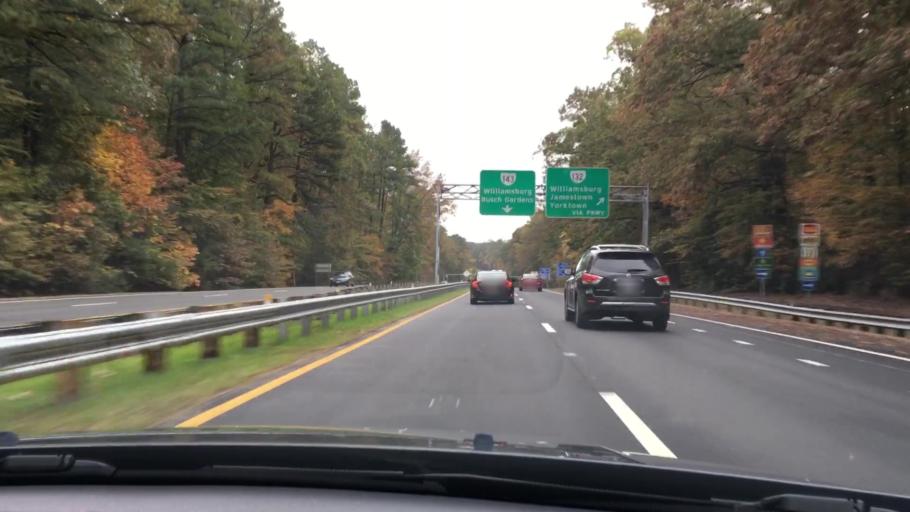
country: US
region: Virginia
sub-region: City of Williamsburg
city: Williamsburg
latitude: 37.2996
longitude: -76.6857
